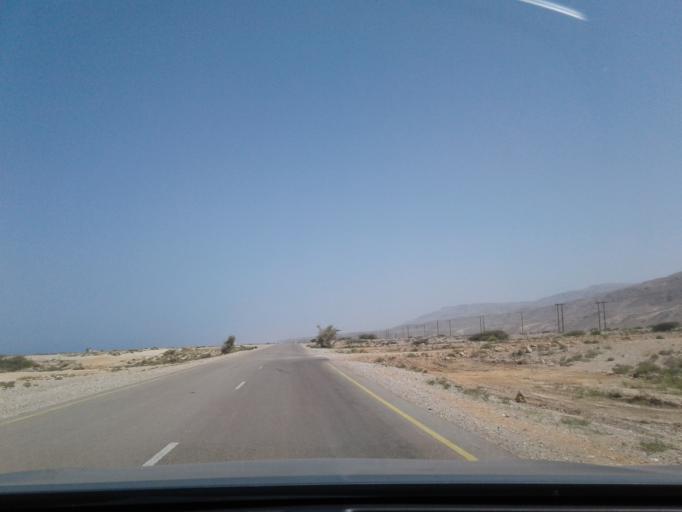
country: OM
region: Ash Sharqiyah
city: Al Qabil
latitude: 23.0401
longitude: 59.0744
